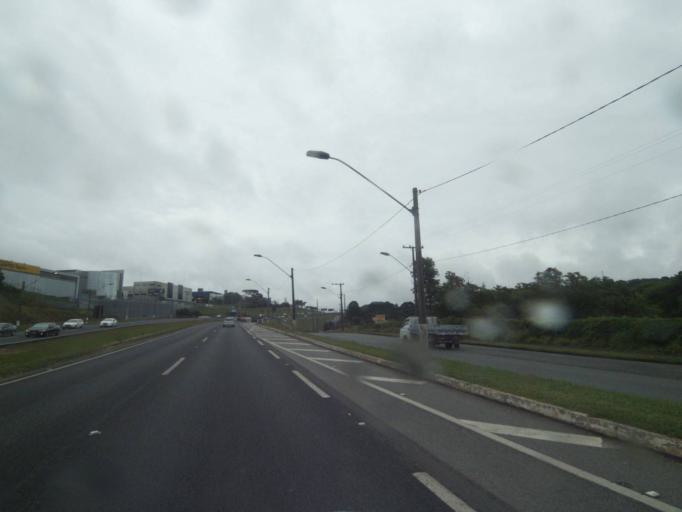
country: BR
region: Parana
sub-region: Curitiba
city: Curitiba
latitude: -25.4305
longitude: -49.3227
